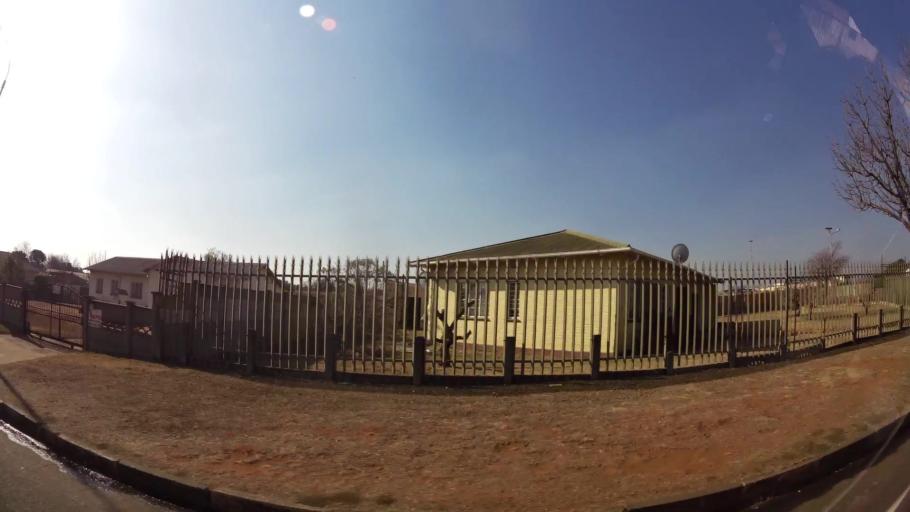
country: ZA
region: Gauteng
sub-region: West Rand District Municipality
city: Randfontein
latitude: -26.1829
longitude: 27.6947
